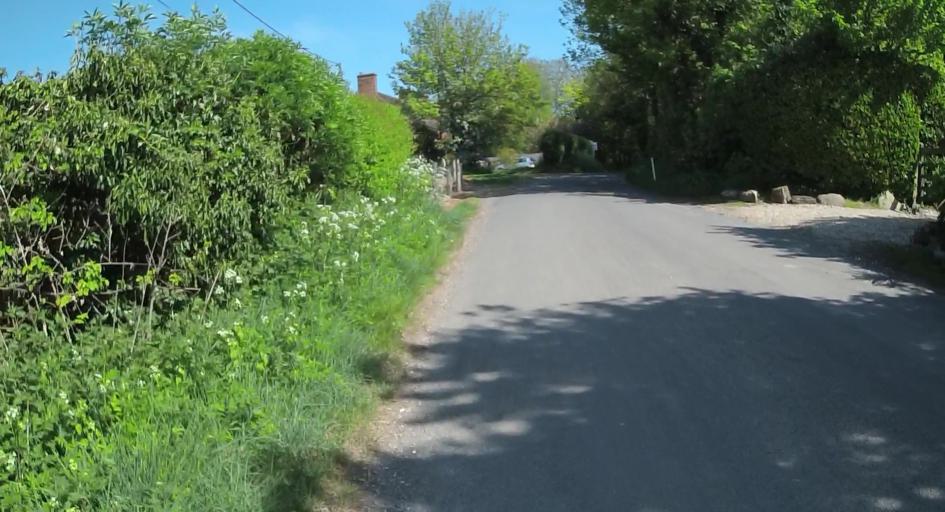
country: GB
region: England
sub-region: Hampshire
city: Kings Worthy
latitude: 51.1510
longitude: -1.2882
